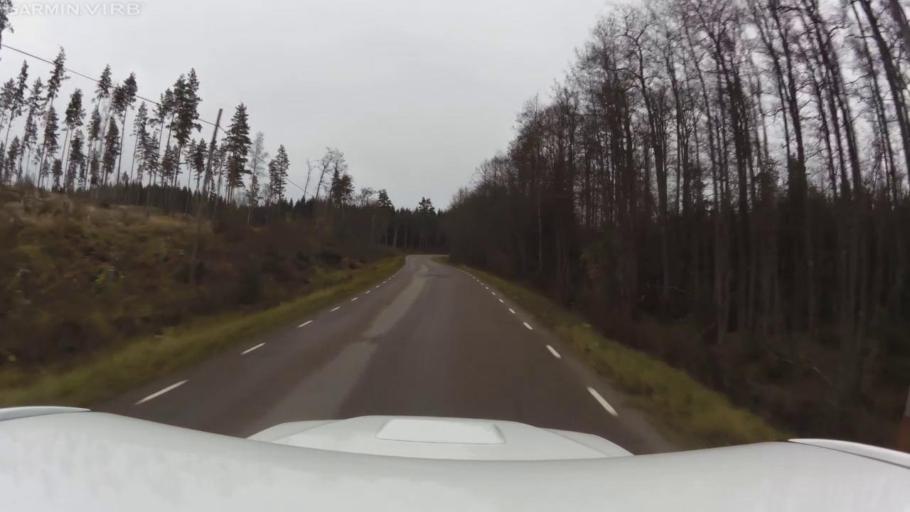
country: SE
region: OEstergoetland
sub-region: Linkopings Kommun
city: Vikingstad
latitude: 58.2400
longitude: 15.3897
